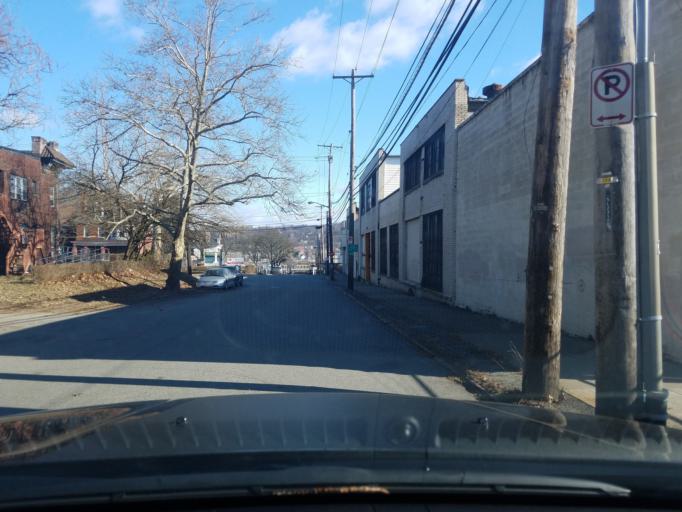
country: US
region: Pennsylvania
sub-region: Allegheny County
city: Wilkinsburg
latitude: 40.4499
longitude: -79.8989
